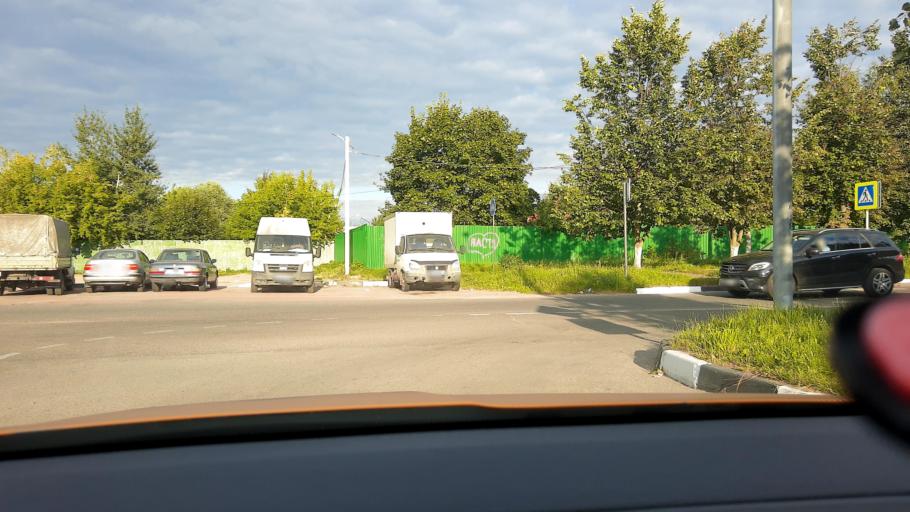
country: RU
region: Moskovskaya
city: Krasnoznamensk
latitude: 55.6042
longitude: 37.0354
